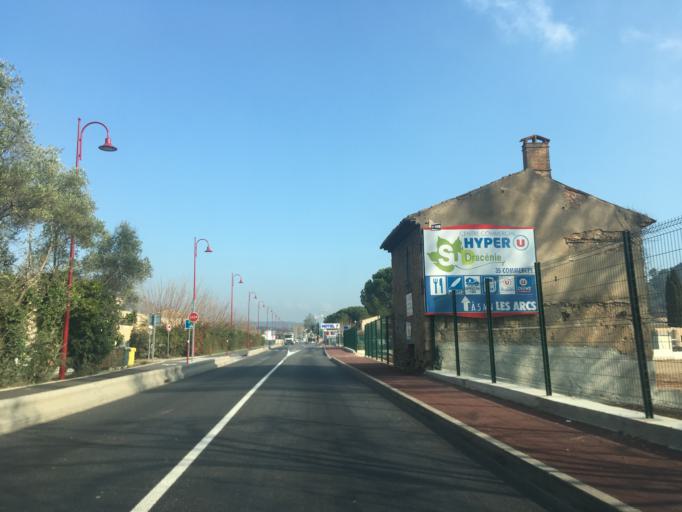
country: FR
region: Provence-Alpes-Cote d'Azur
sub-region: Departement du Var
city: Vidauban
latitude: 43.4182
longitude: 6.4226
